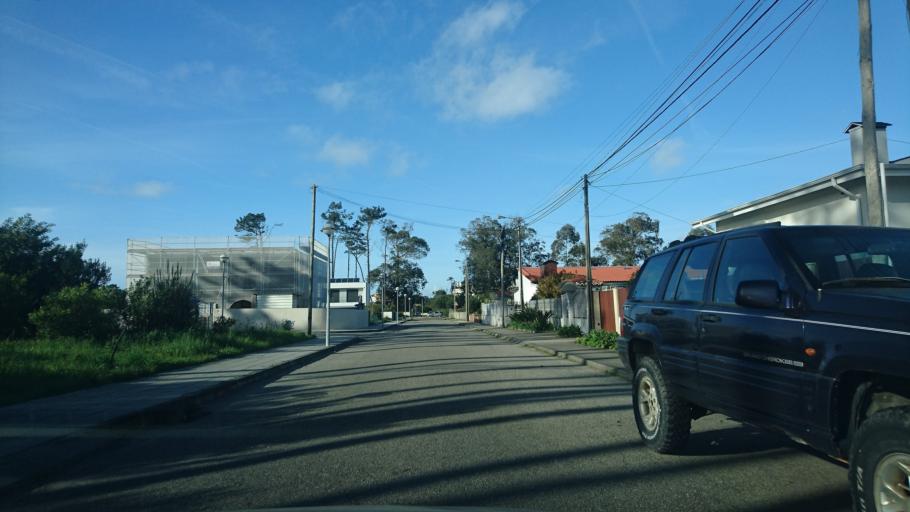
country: PT
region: Aveiro
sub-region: Ovar
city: Esmoriz
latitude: 40.9552
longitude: -8.6457
